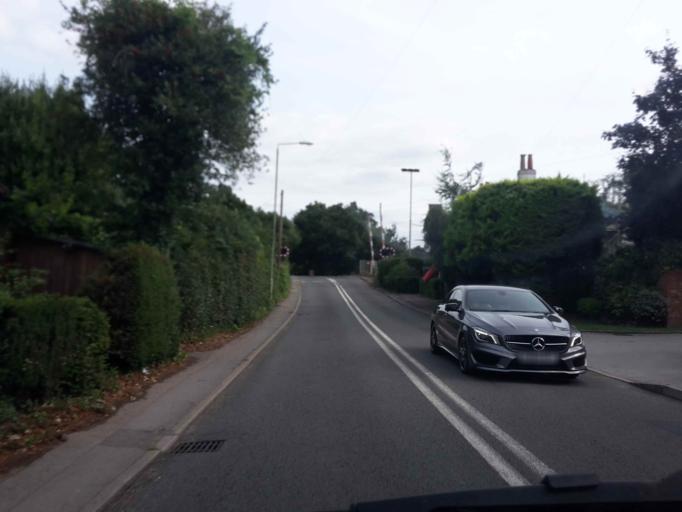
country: GB
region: England
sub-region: Wokingham
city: Wokingham
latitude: 51.4047
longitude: -0.8210
